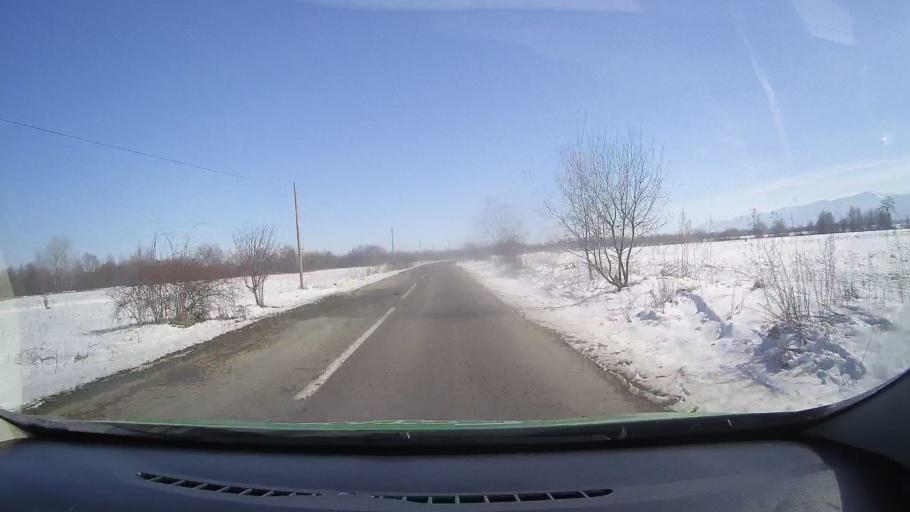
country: RO
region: Brasov
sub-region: Comuna Recea
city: Recea
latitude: 45.7306
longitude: 24.9627
